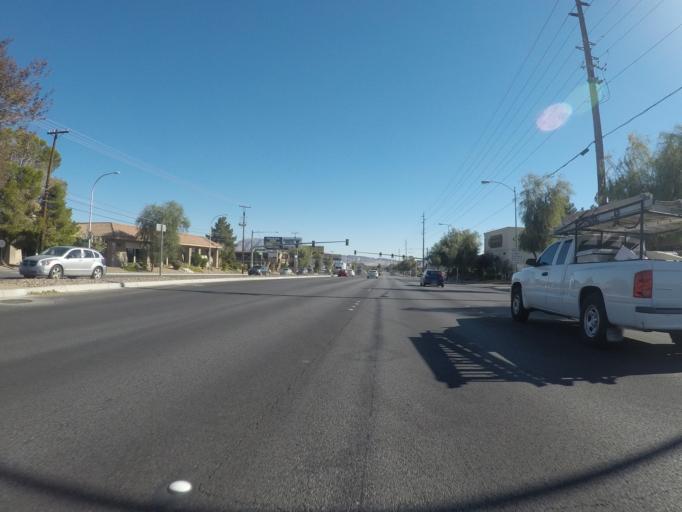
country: US
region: Nevada
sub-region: Clark County
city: Winchester
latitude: 36.1443
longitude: -115.1244
